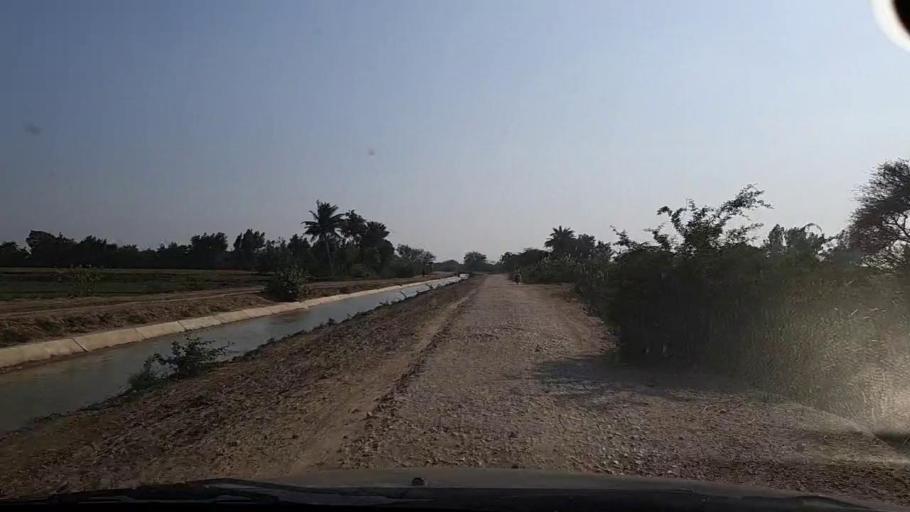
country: PK
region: Sindh
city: Mirpur Sakro
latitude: 24.3146
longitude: 67.7027
